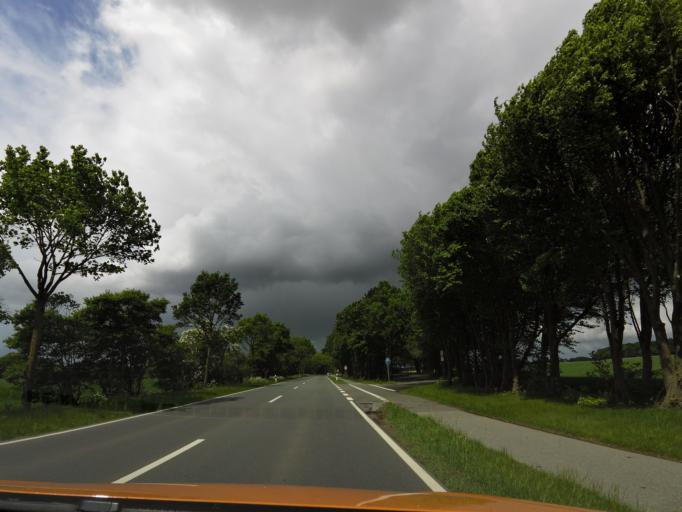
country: DE
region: Lower Saxony
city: Ganderkesee
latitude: 53.0708
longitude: 8.5277
